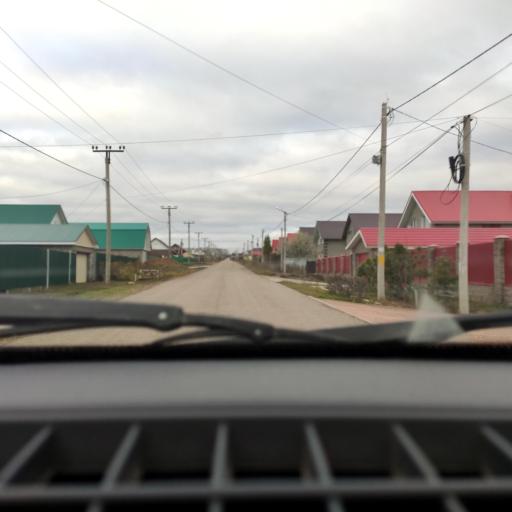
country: RU
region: Bashkortostan
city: Avdon
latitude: 54.6569
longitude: 55.7460
